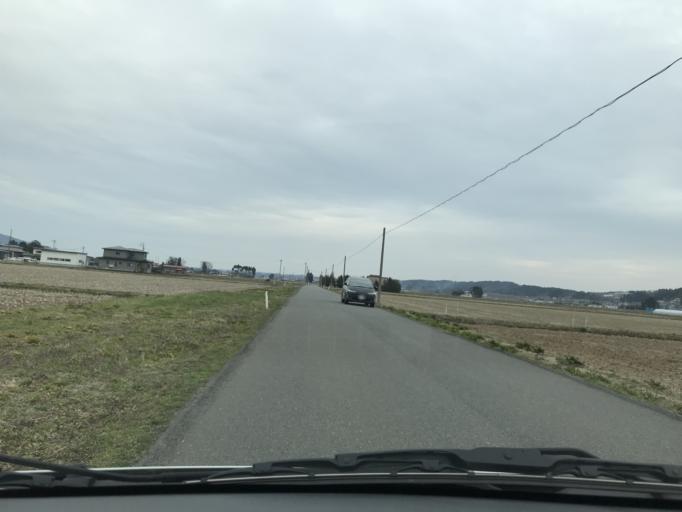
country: JP
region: Iwate
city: Mizusawa
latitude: 39.0806
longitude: 141.1436
